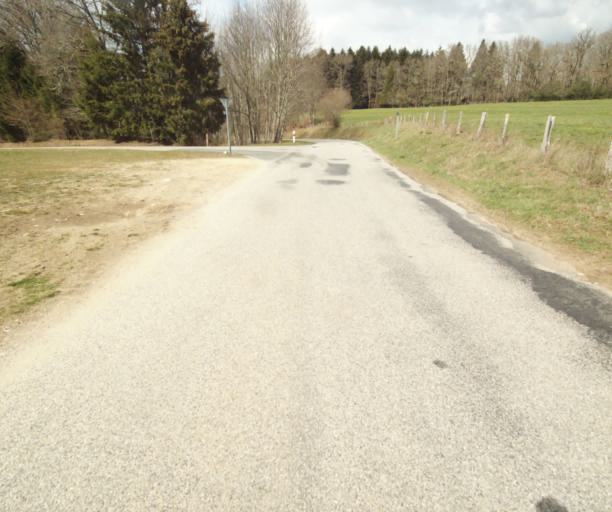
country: FR
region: Limousin
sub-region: Departement de la Correze
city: Correze
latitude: 45.2715
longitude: 1.9768
